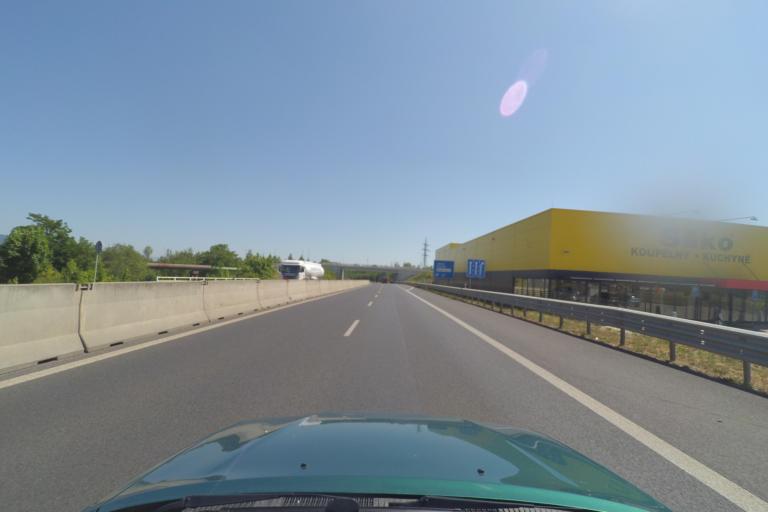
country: CZ
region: Ustecky
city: Jirkov
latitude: 50.4873
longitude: 13.4476
